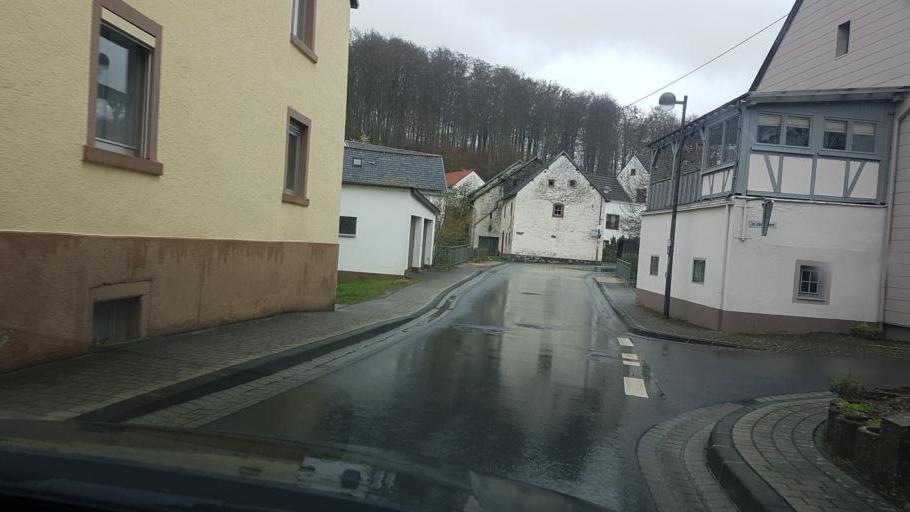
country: DE
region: Rheinland-Pfalz
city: Berlingen
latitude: 50.2389
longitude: 6.7195
